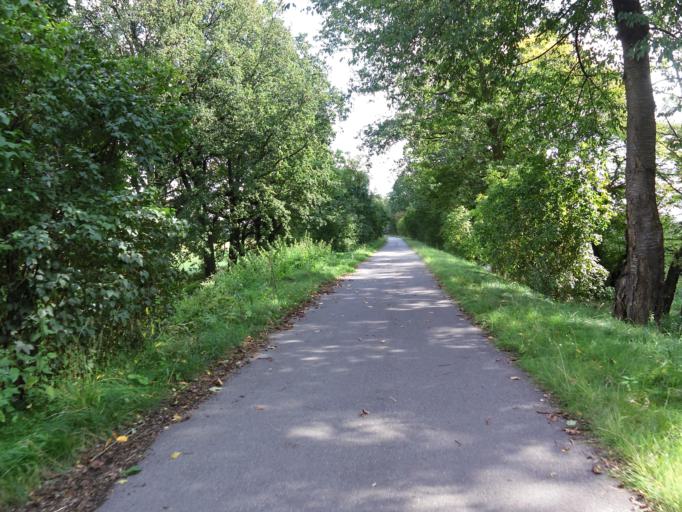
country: DE
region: Saxony-Anhalt
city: Vockerode
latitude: 51.8441
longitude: 12.3683
